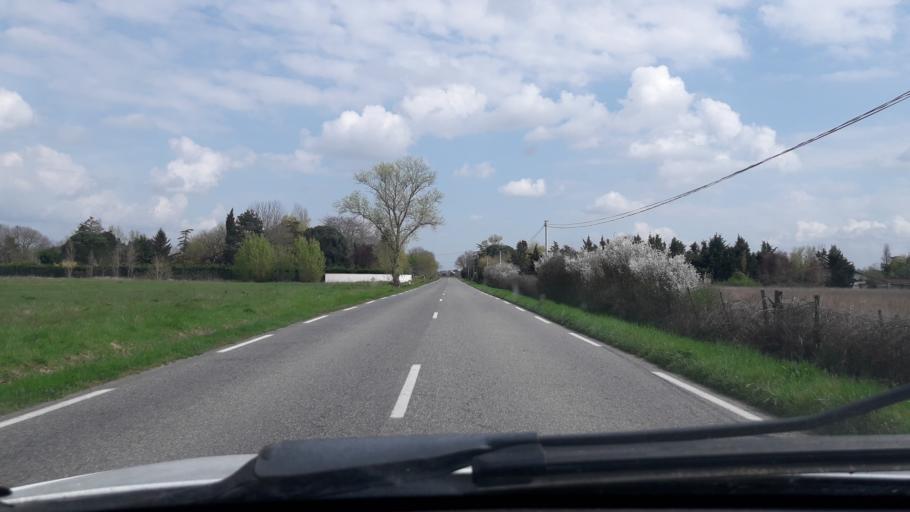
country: FR
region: Midi-Pyrenees
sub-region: Departement de la Haute-Garonne
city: Seysses
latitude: 43.5014
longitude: 1.2762
